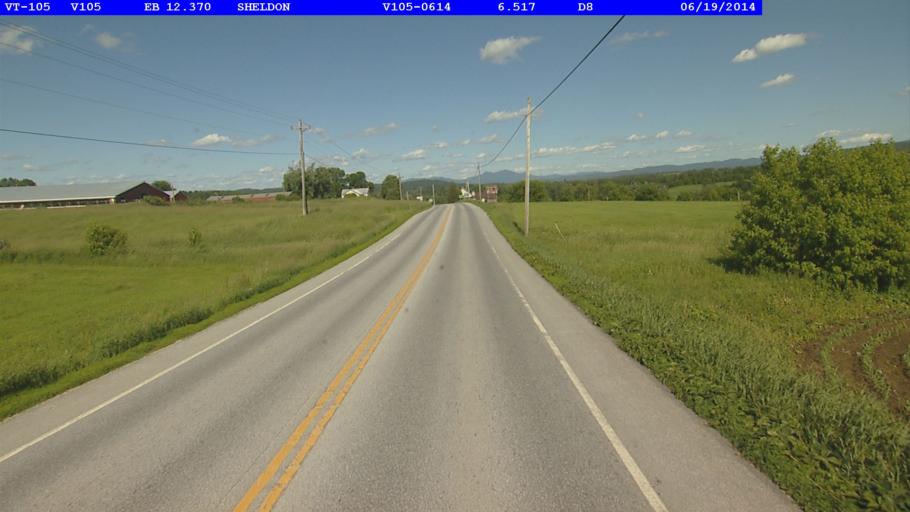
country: US
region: Vermont
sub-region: Franklin County
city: Enosburg Falls
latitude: 44.9098
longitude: -72.9087
